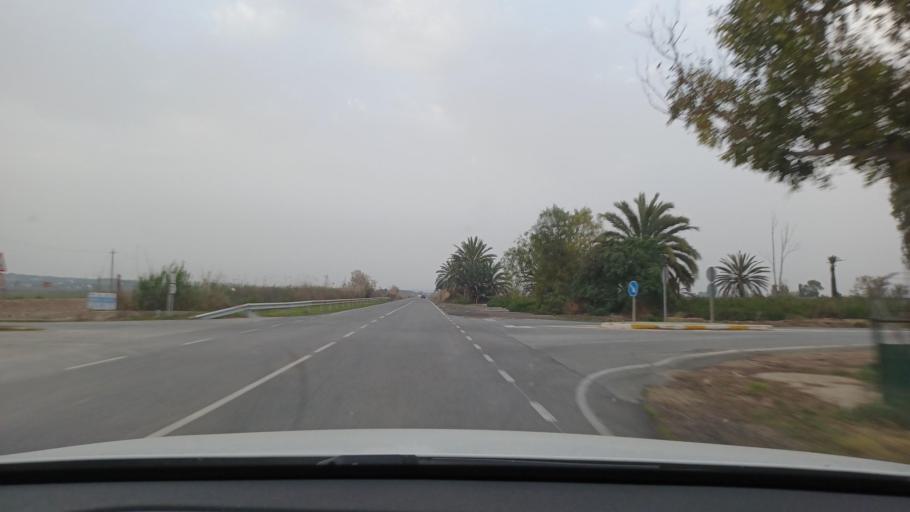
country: ES
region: Valencia
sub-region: Provincia de Alicante
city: Daya Vieja
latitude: 38.1668
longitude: -0.7026
